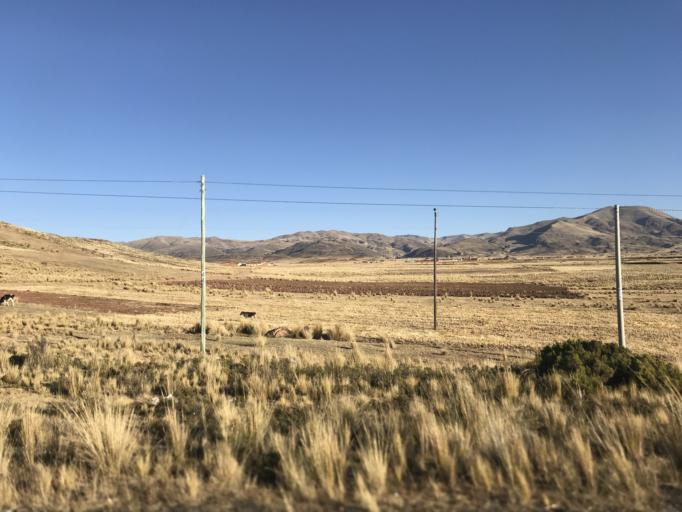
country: BO
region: La Paz
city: Tiahuanaco
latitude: -16.5667
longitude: -68.6475
